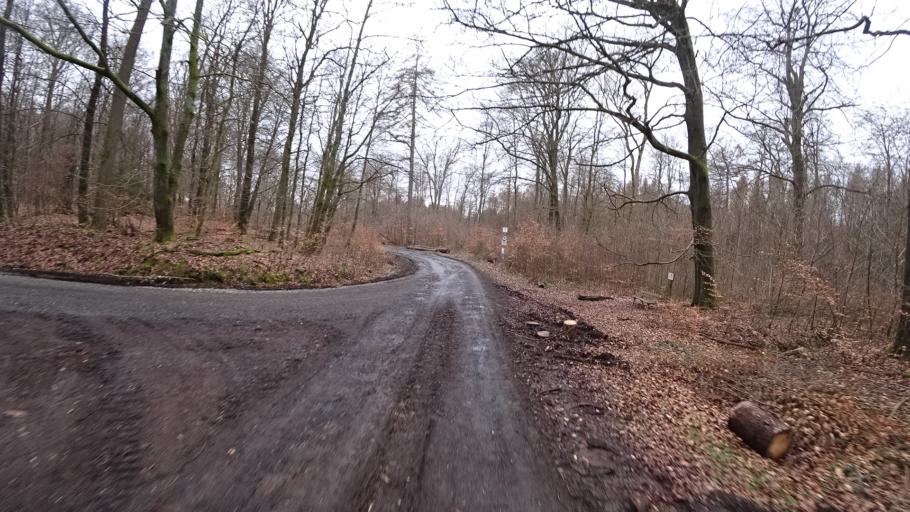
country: DE
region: Rheinland-Pfalz
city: Hilgert
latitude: 50.4363
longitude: 7.7007
